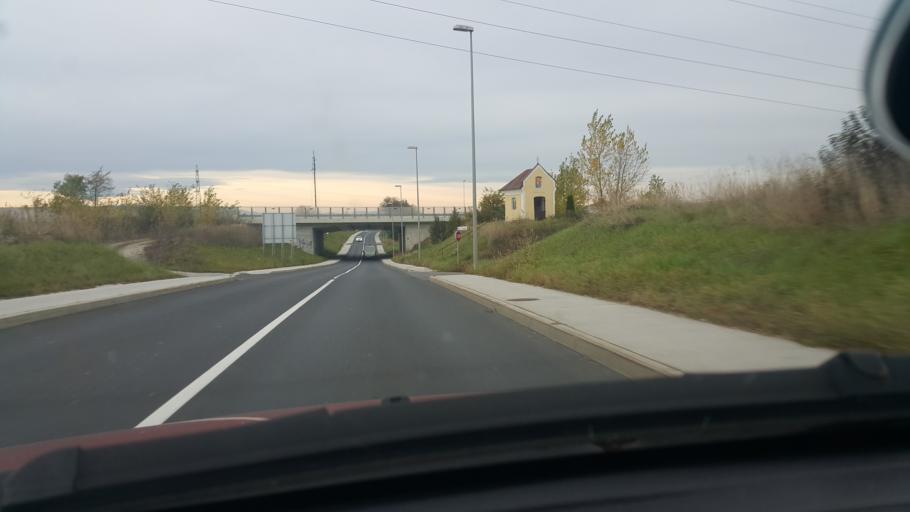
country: SI
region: Miklavz na Dravskem Polju
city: Miklavz na Dravskem Polju
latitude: 46.5274
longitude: 15.6993
